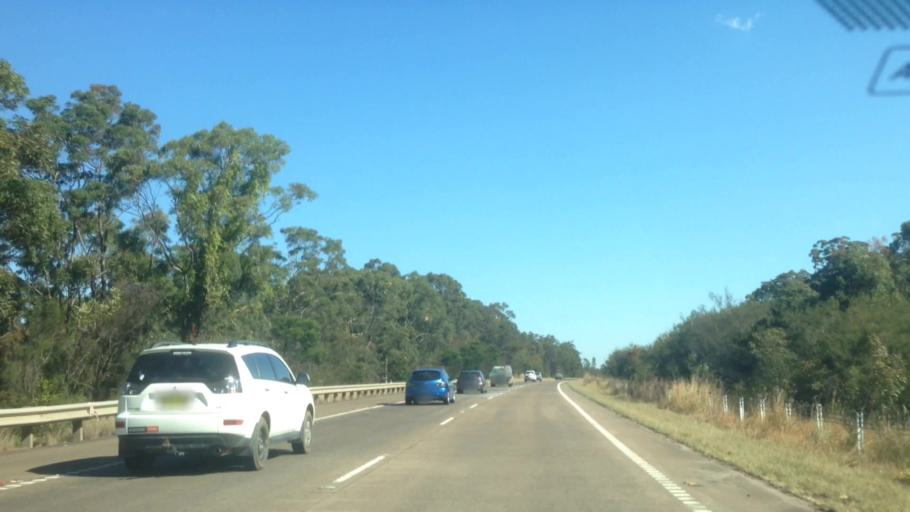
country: AU
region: New South Wales
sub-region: Wyong Shire
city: Charmhaven
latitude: -33.1966
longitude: 151.4649
